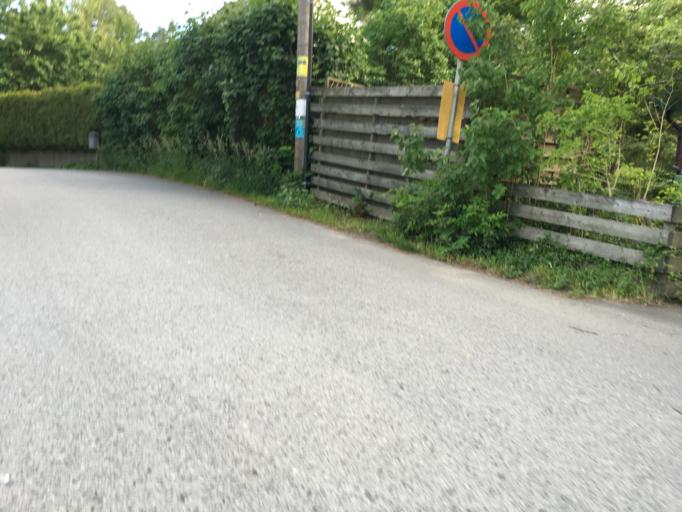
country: SE
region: Stockholm
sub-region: Nacka Kommun
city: Fisksatra
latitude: 59.3180
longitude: 18.2375
